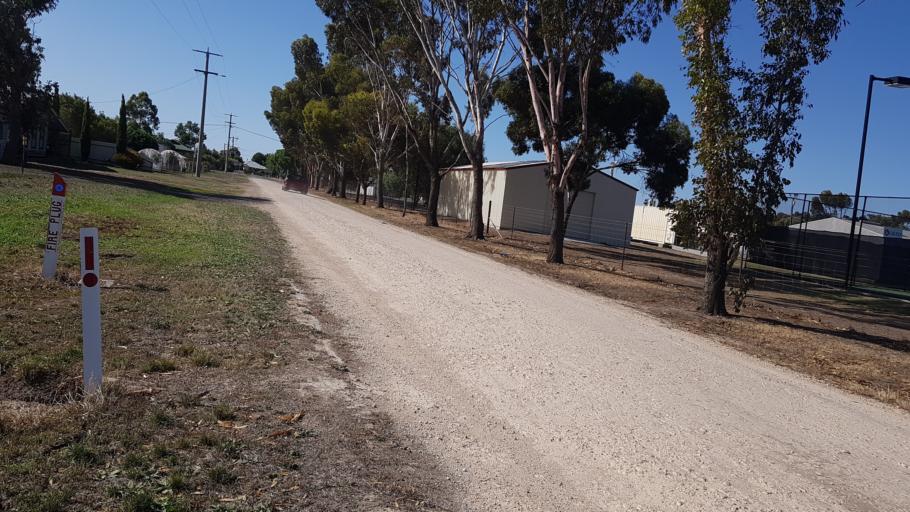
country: AU
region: Victoria
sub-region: Horsham
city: Horsham
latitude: -36.7433
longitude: 141.9473
